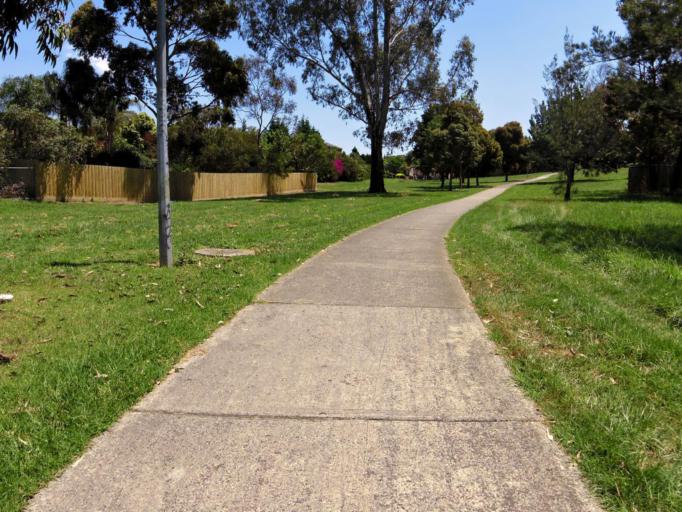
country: AU
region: Victoria
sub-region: Casey
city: Endeavour Hills
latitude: -37.9816
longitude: 145.2628
